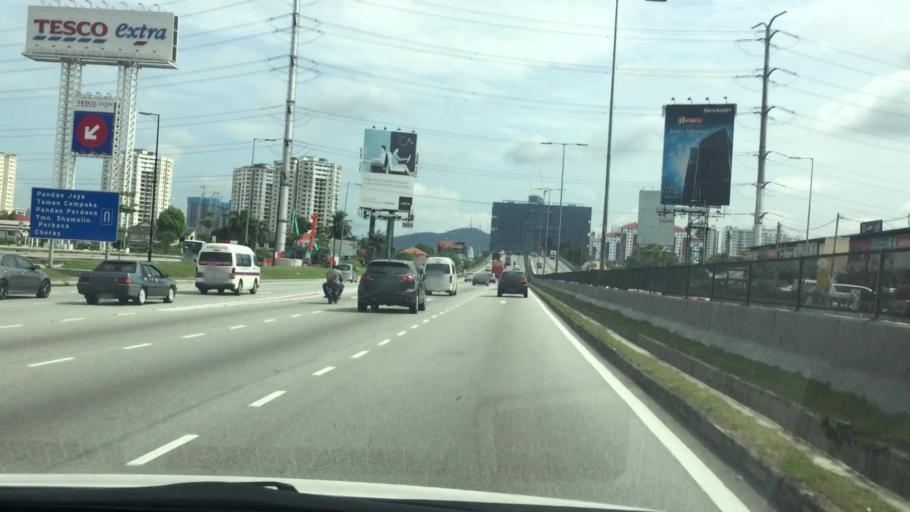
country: MY
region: Kuala Lumpur
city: Kuala Lumpur
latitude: 3.1428
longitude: 101.7434
